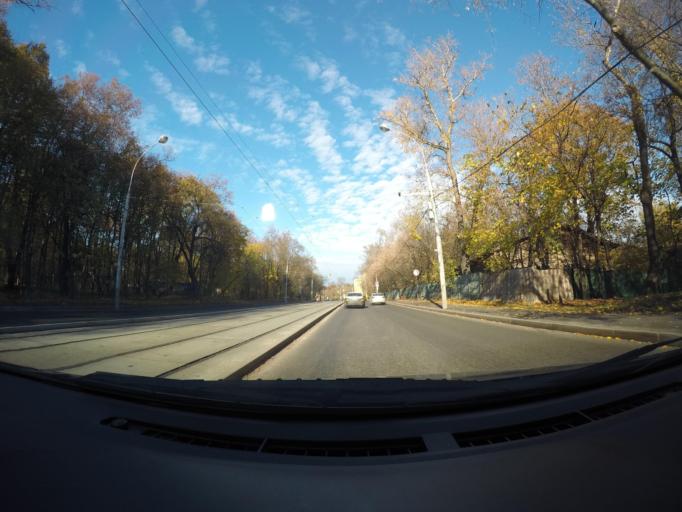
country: RU
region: Moscow
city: Sokol'niki
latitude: 55.8162
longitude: 37.6819
